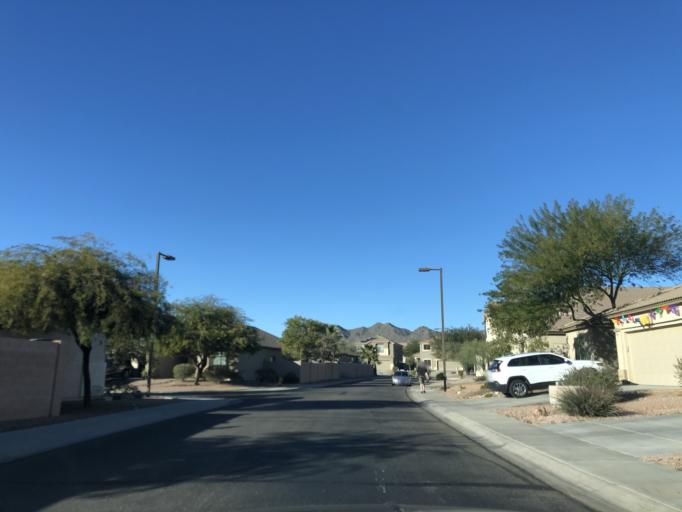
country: US
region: Arizona
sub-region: Maricopa County
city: Buckeye
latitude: 33.4377
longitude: -112.5692
